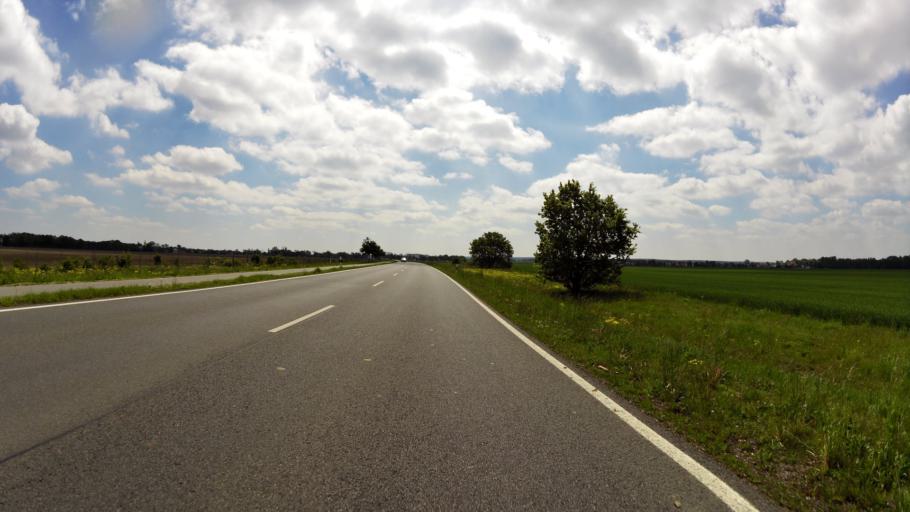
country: DE
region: Saxony
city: Torgau
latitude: 51.5220
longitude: 13.0301
